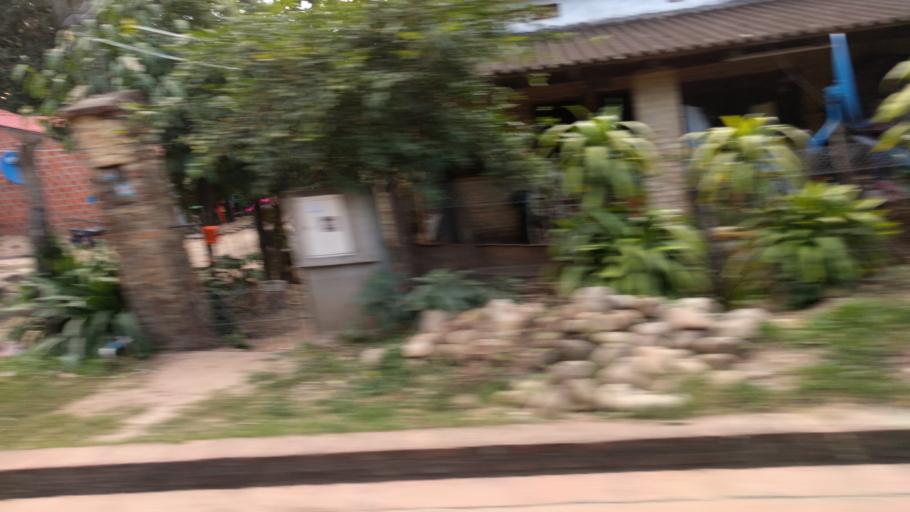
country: BO
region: Santa Cruz
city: Buena Vista
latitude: -17.4575
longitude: -63.6579
